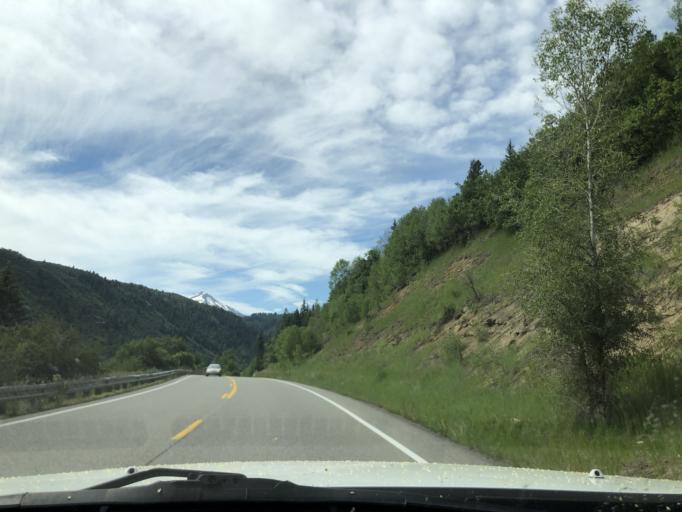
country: US
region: Colorado
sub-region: Delta County
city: Paonia
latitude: 38.9747
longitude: -107.3422
